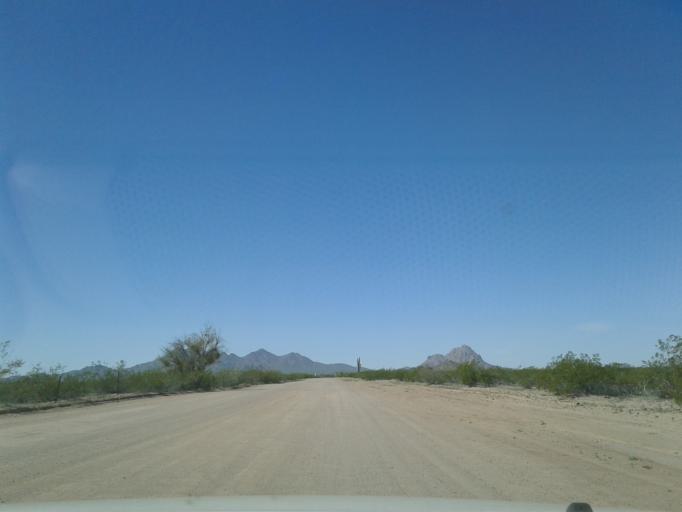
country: US
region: Arizona
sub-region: Pima County
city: Avra Valley
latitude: 32.4293
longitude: -111.3749
